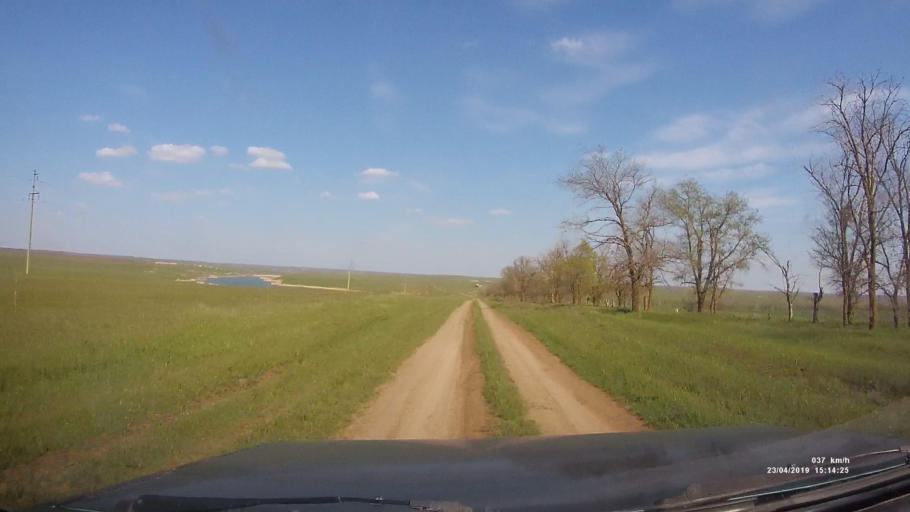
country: RU
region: Rostov
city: Remontnoye
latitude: 46.5397
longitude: 42.9632
